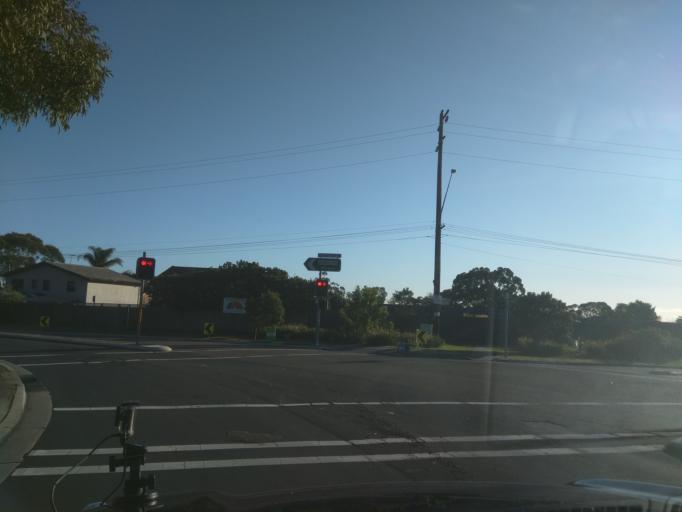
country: AU
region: New South Wales
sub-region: Sutherland Shire
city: Woronora Heights
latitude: -34.0205
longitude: 151.0358
